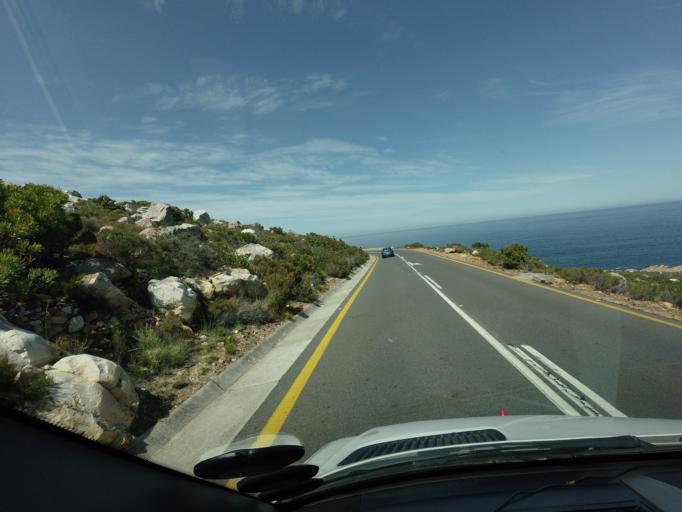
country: ZA
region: Western Cape
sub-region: Overberg District Municipality
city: Grabouw
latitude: -34.2166
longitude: 18.8341
